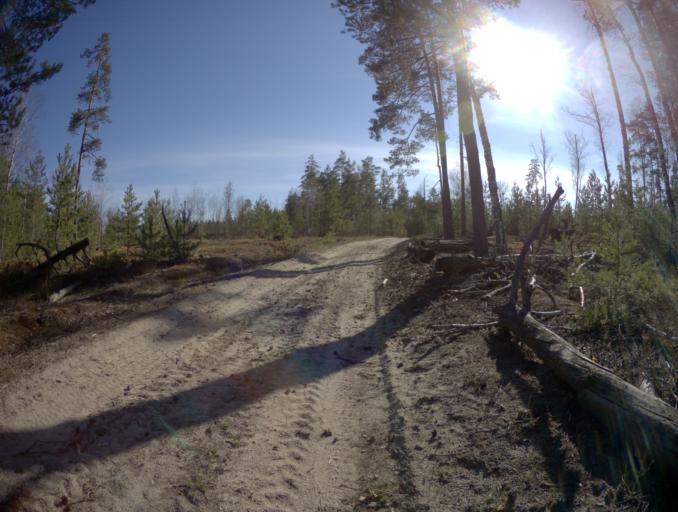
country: RU
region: Vladimir
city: Ivanishchi
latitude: 55.7003
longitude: 40.4361
